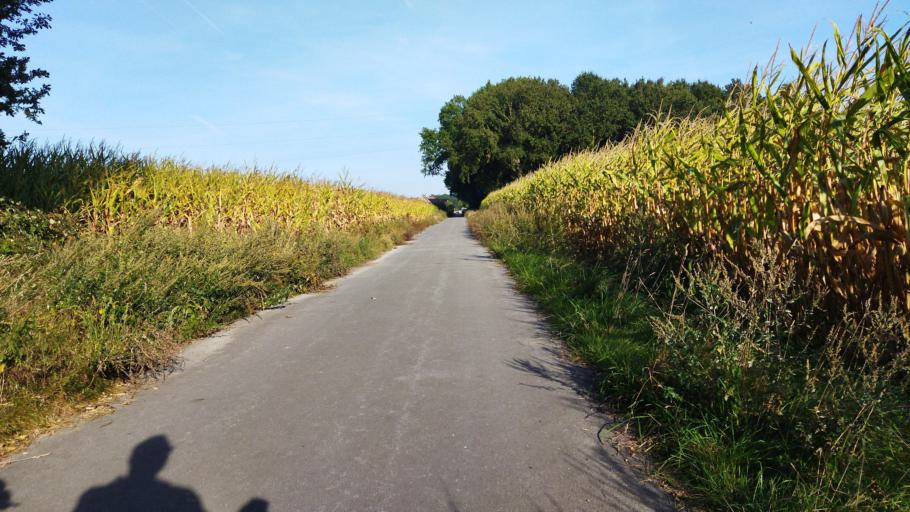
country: DE
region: Lower Saxony
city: Bad Laer
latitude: 52.0996
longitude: 8.0517
